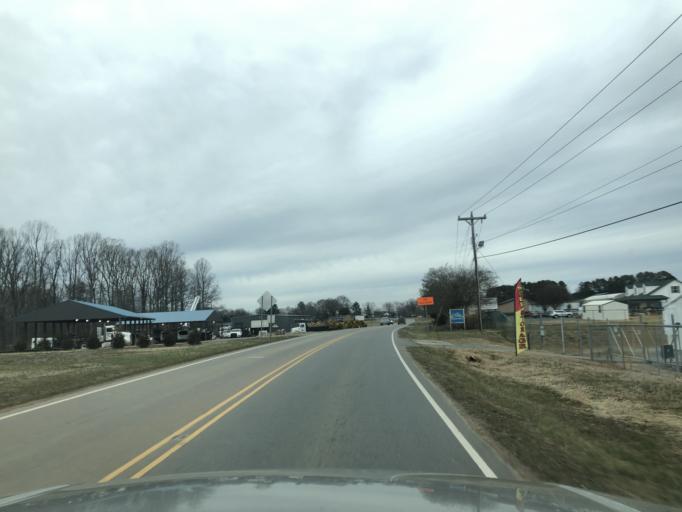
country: US
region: North Carolina
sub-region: Cleveland County
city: Shelby
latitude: 35.3225
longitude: -81.4960
